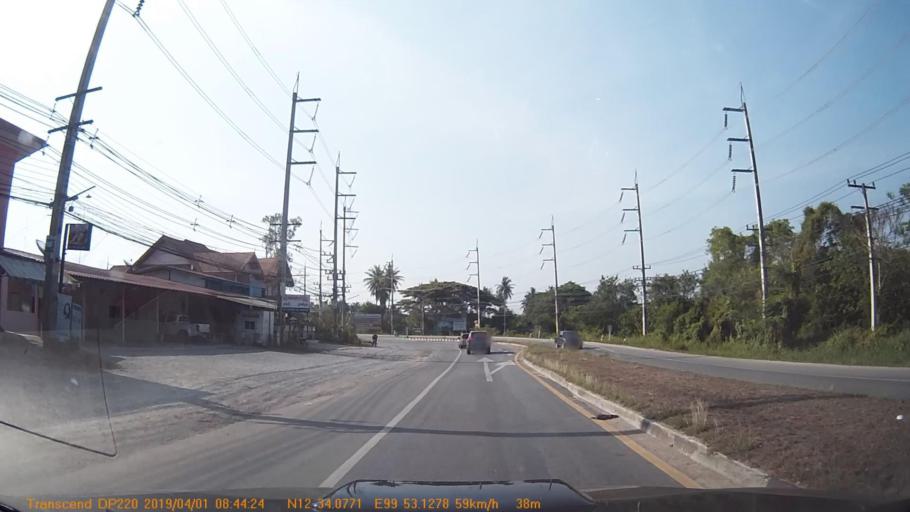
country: TH
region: Prachuap Khiri Khan
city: Hua Hin
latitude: 12.5678
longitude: 99.8855
